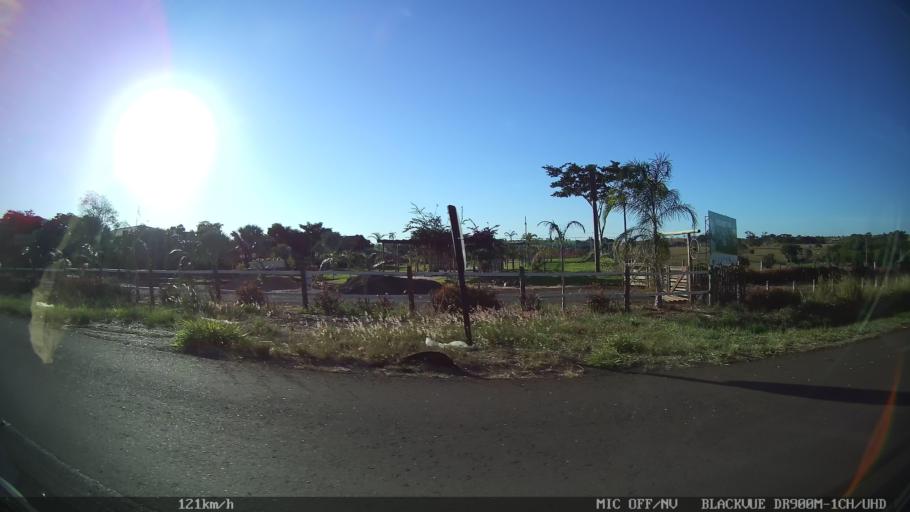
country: BR
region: Sao Paulo
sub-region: Guapiacu
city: Guapiacu
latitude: -20.7883
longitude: -49.2874
